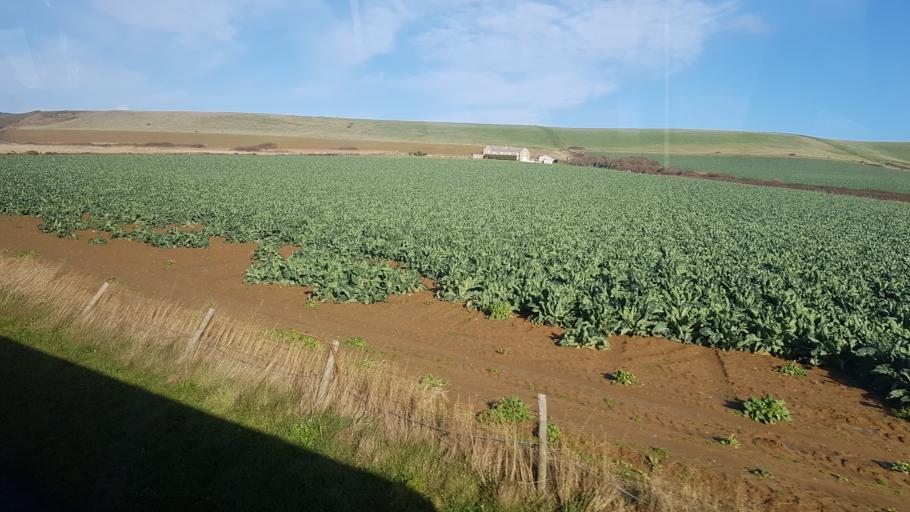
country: GB
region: England
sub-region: Isle of Wight
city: Freshwater
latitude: 50.6559
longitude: -1.4674
